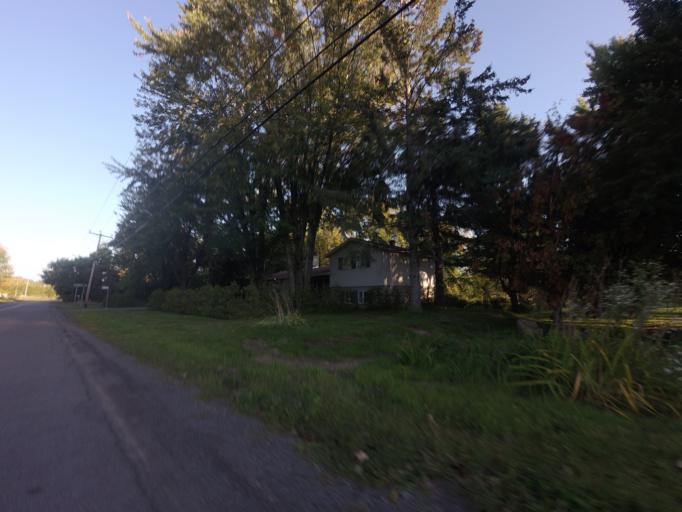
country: CA
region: Quebec
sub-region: Monteregie
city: Rigaud
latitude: 45.4808
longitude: -74.2504
